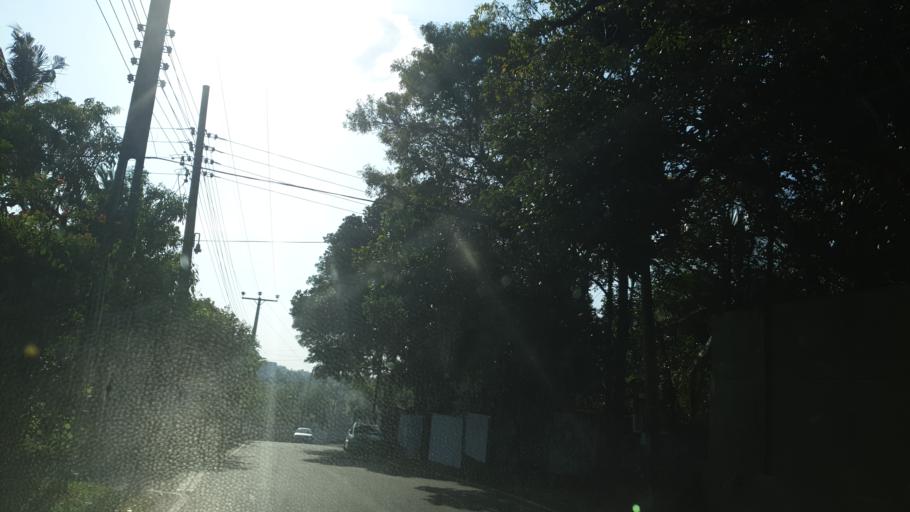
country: LK
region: Western
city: Battaramulla South
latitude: 6.8808
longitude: 79.9359
